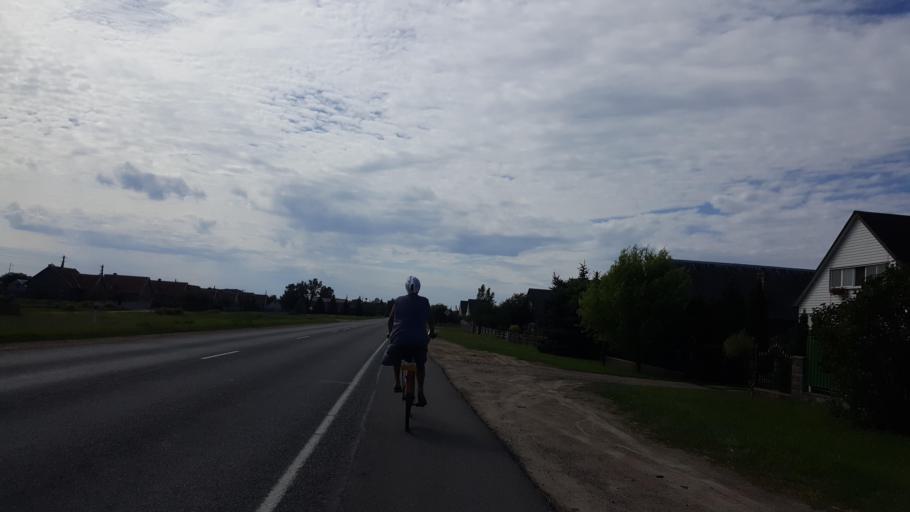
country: BY
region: Brest
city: Kamyanyets
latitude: 52.3268
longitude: 23.9168
